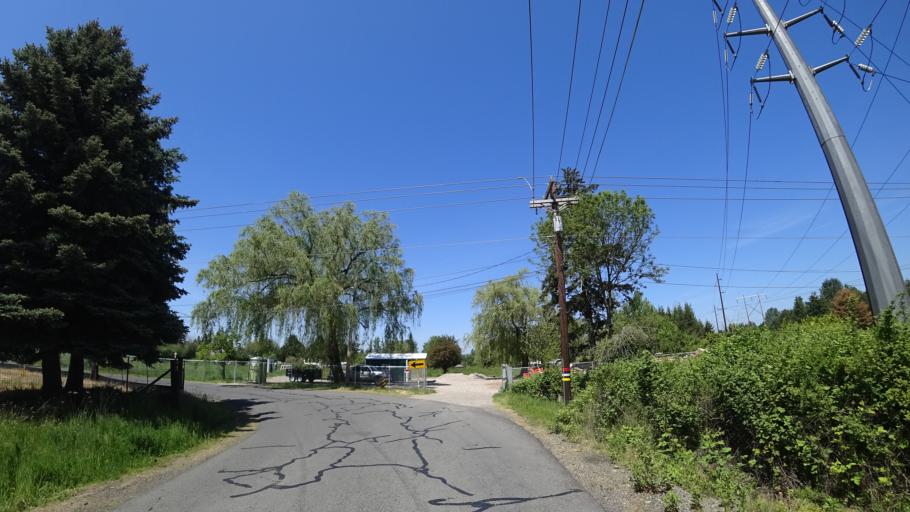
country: US
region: Oregon
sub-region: Clackamas County
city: Happy Valley
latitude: 45.4609
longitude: -122.4865
